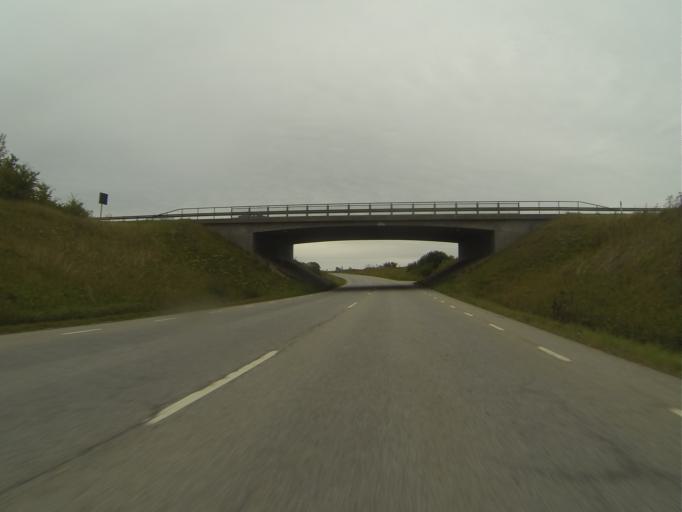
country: SE
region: Skane
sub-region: Svedala Kommun
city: Klagerup
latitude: 55.6442
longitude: 13.2667
